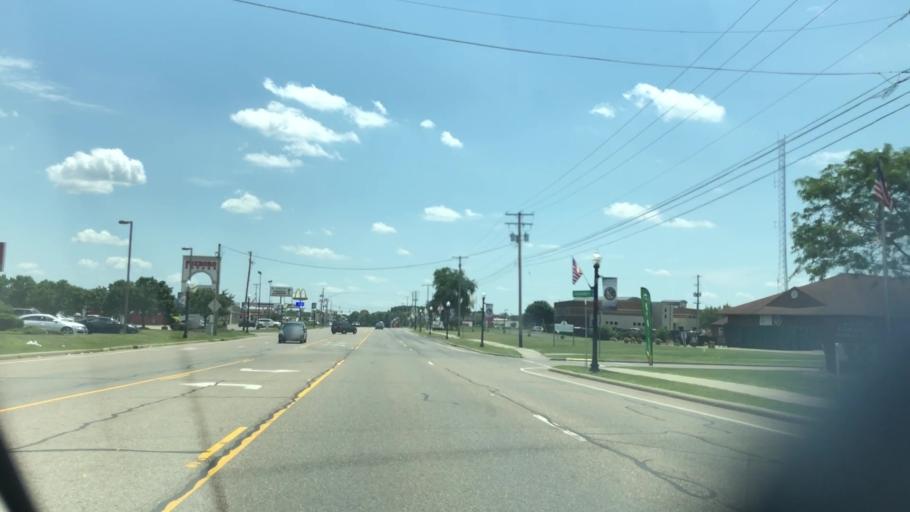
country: US
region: Ohio
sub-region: Stark County
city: Perry Heights
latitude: 40.8636
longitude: -81.4850
